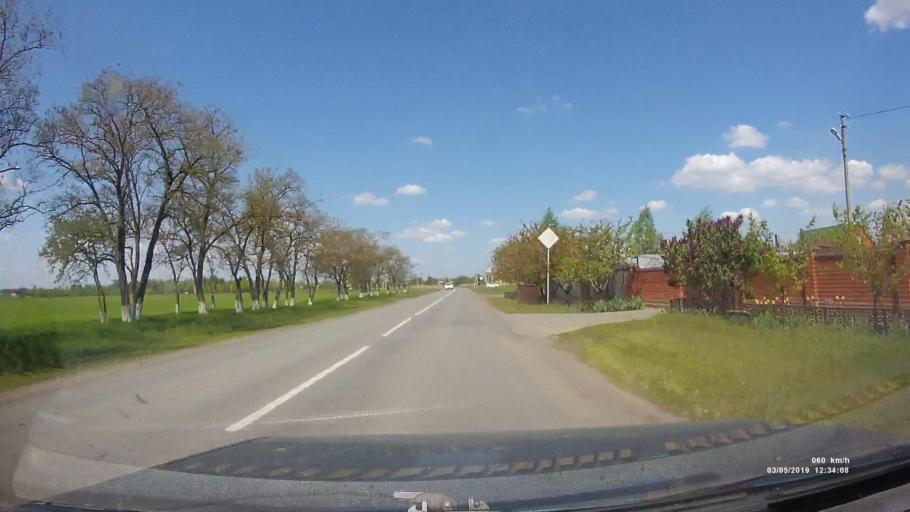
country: RU
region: Rostov
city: Semikarakorsk
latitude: 47.5192
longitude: 40.7698
